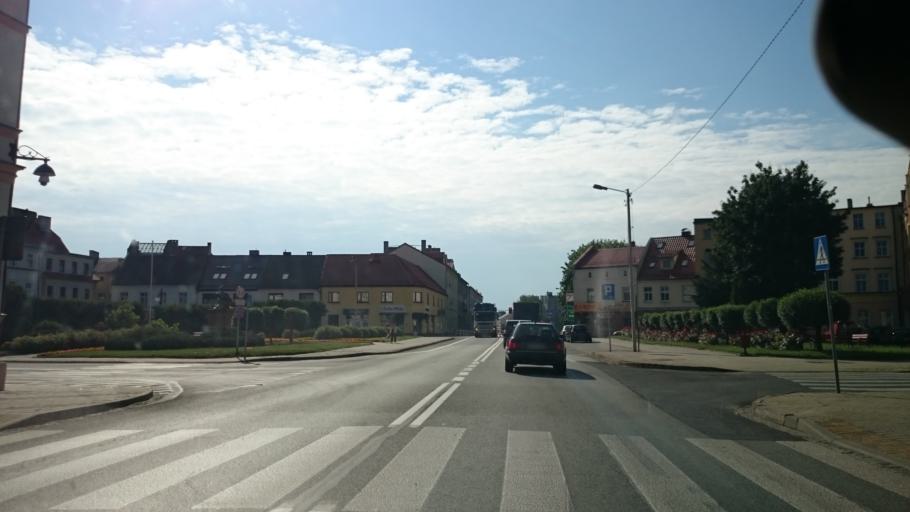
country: PL
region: Opole Voivodeship
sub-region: Powiat strzelecki
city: Strzelce Opolskie
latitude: 50.5107
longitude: 18.3004
